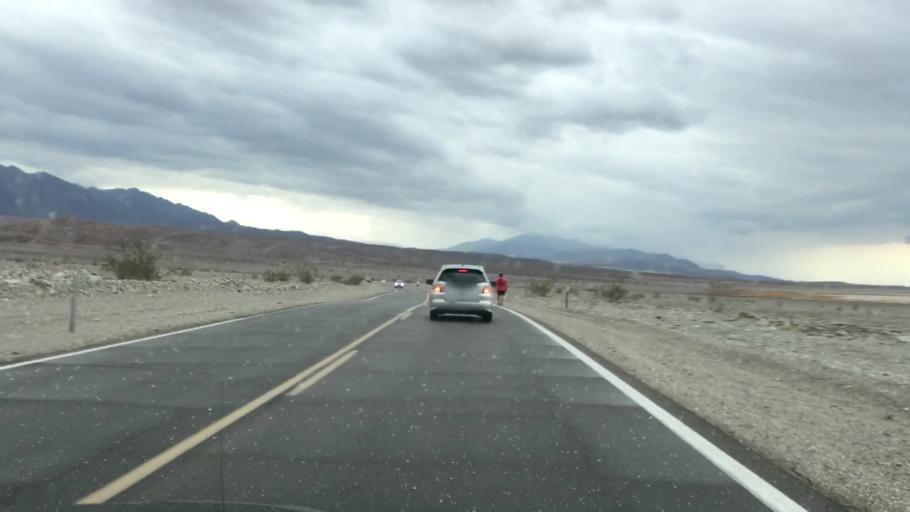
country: US
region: Nevada
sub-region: Nye County
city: Beatty
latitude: 36.5472
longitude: -116.8900
